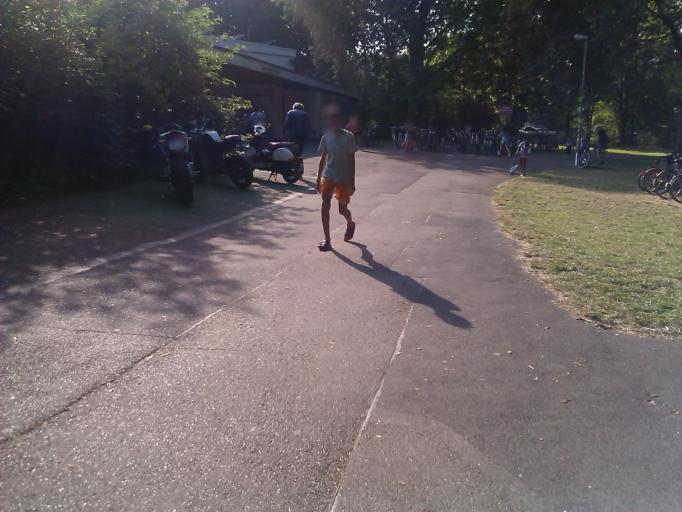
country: DE
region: Baden-Wuerttemberg
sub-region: Regierungsbezirk Stuttgart
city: Heilbronn
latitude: 49.1326
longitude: 9.2070
